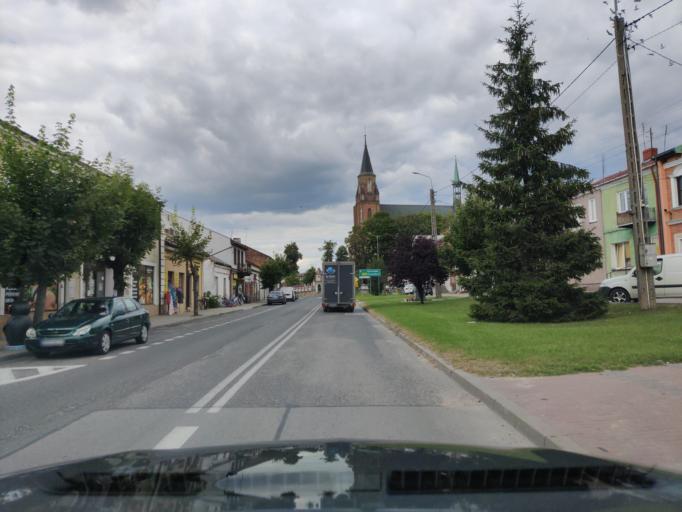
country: PL
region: Masovian Voivodeship
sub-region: Powiat sokolowski
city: Kosow Lacki
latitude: 52.5949
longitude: 22.1469
